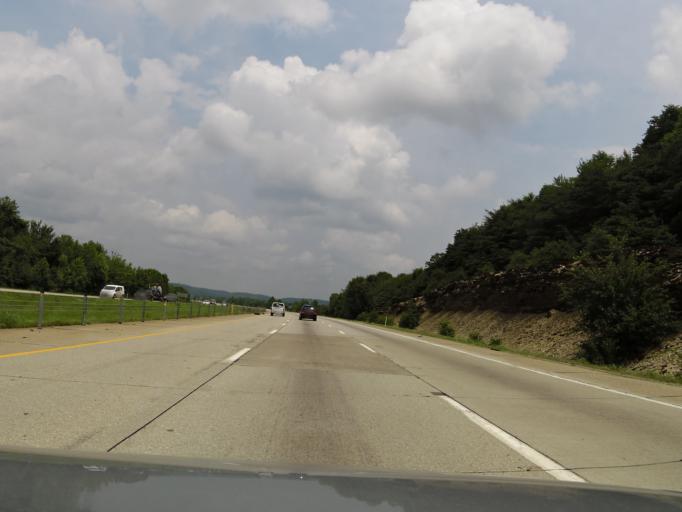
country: US
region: Kentucky
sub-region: Bullitt County
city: Shepherdsville
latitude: 37.9110
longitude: -85.6885
